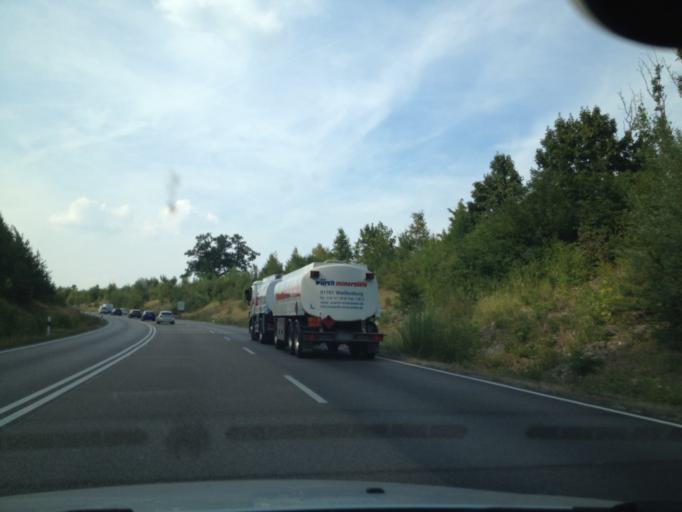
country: DE
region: Bavaria
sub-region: Swabia
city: Kaisheim
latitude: 48.7613
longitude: 10.7807
